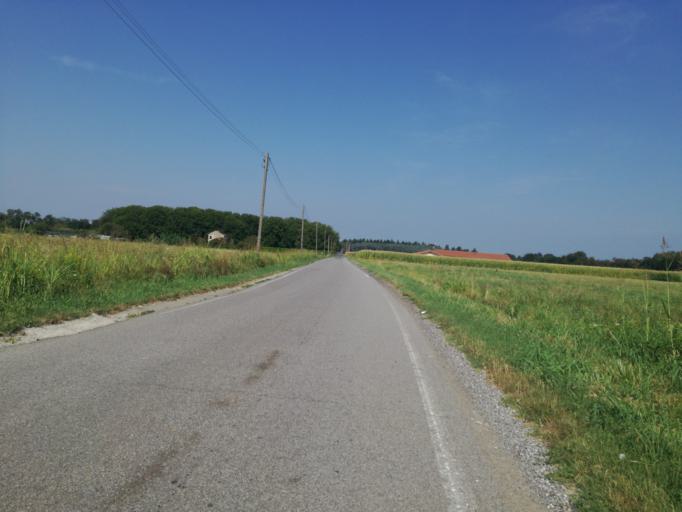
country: IT
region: Lombardy
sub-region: Provincia di Monza e Brianza
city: Cornate d'Adda
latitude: 45.6256
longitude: 9.4865
